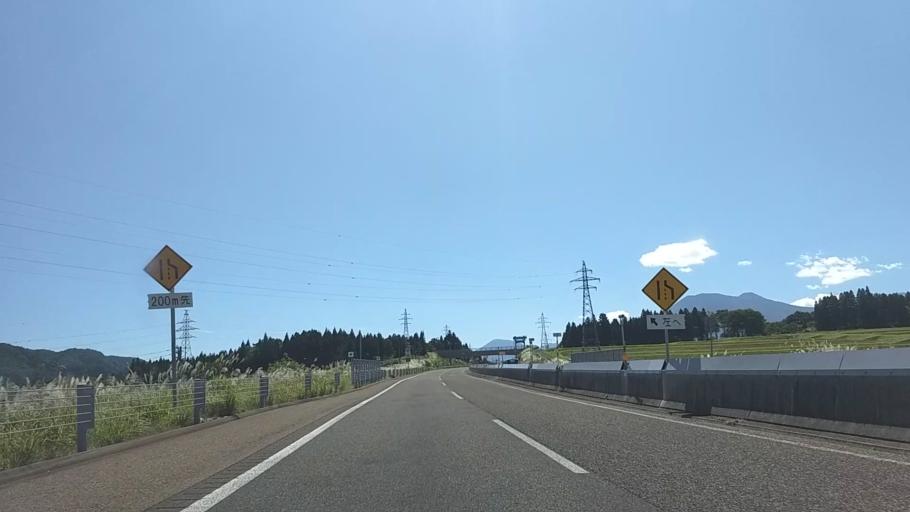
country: JP
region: Niigata
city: Arai
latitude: 36.9144
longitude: 138.2154
